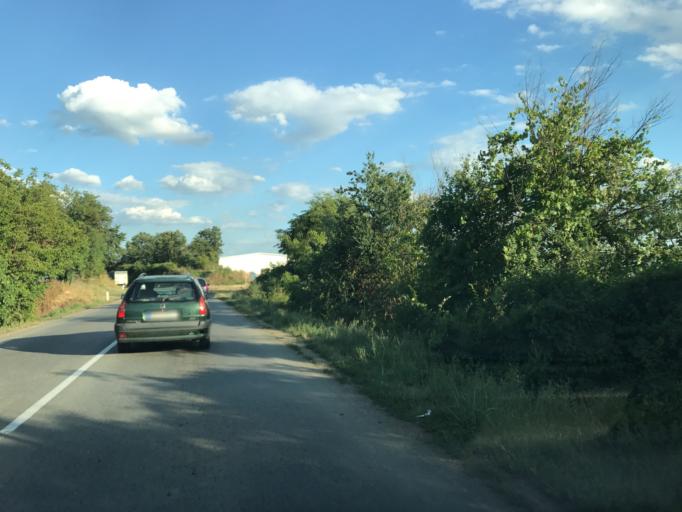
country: RS
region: Central Serbia
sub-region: Belgrade
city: Grocka
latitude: 44.6999
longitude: 20.6627
